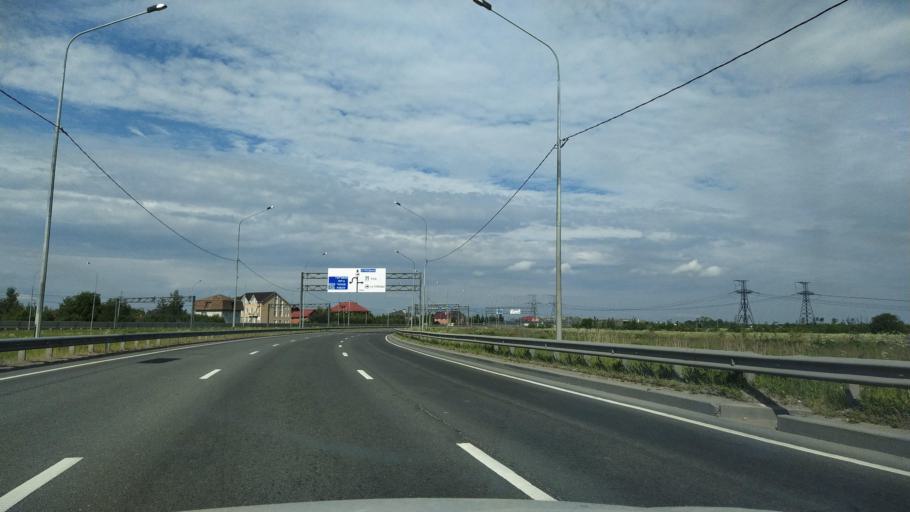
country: RU
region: St.-Petersburg
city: Aleksandrovskaya
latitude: 59.7411
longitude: 30.3225
